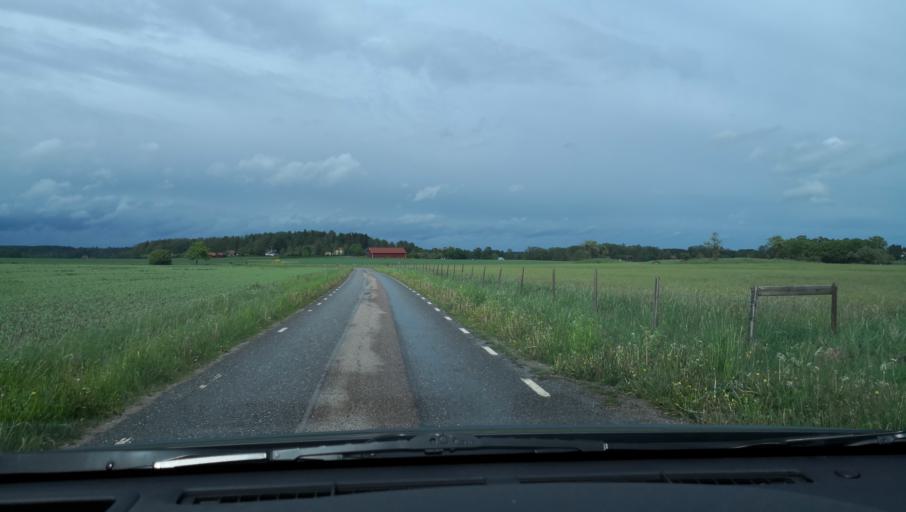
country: SE
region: Uppsala
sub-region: Enkopings Kommun
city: Orsundsbro
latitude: 59.7133
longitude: 17.4231
